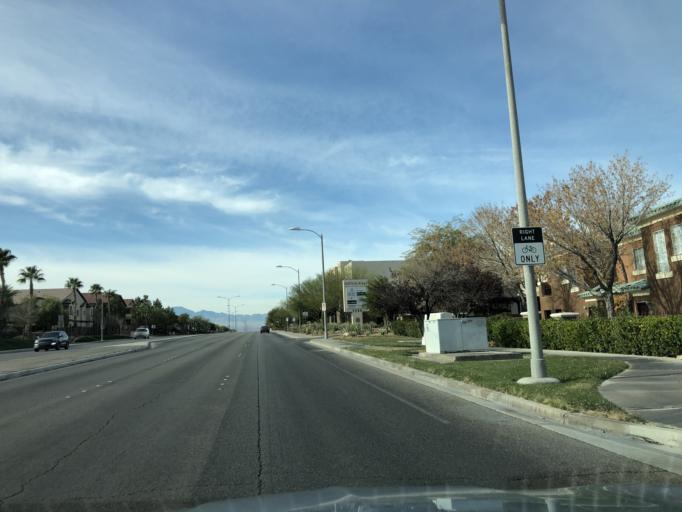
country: US
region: Nevada
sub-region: Clark County
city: Whitney
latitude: 36.0060
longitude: -115.0861
